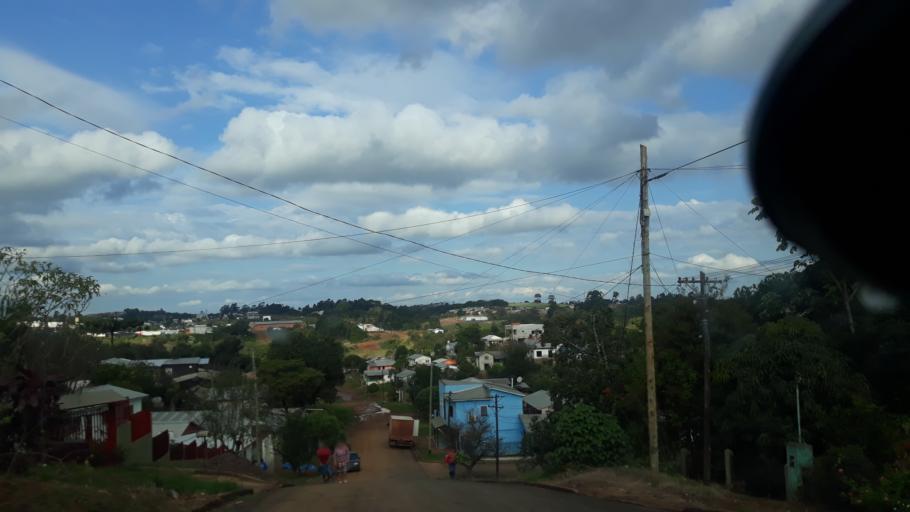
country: AR
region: Misiones
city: Bernardo de Irigoyen
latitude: -26.2631
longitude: -53.6465
